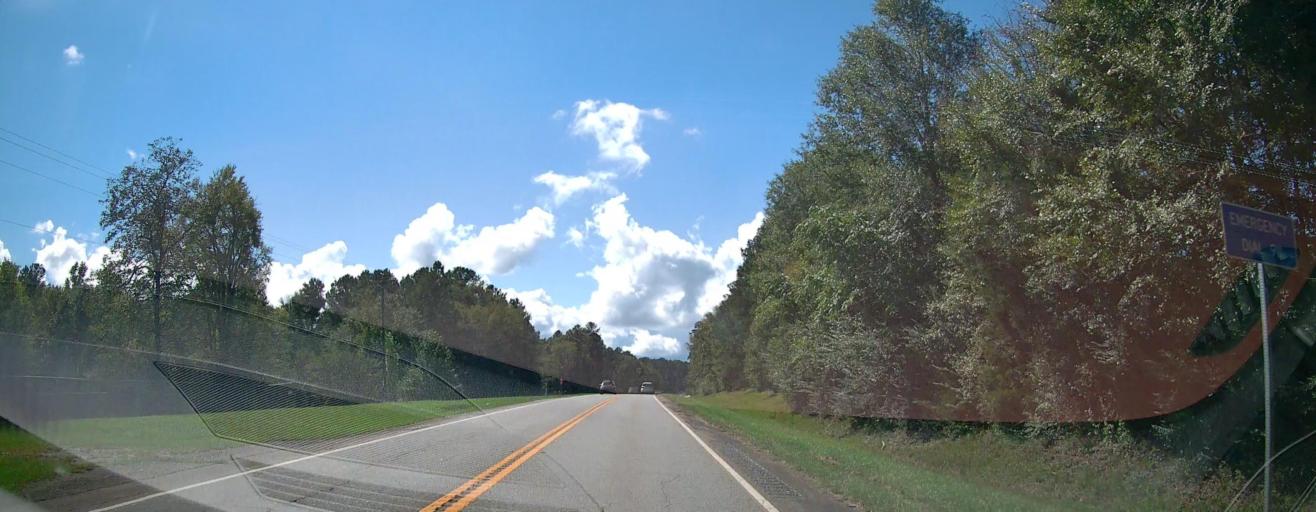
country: US
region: Georgia
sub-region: Jones County
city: Gray
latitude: 33.0415
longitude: -83.3974
